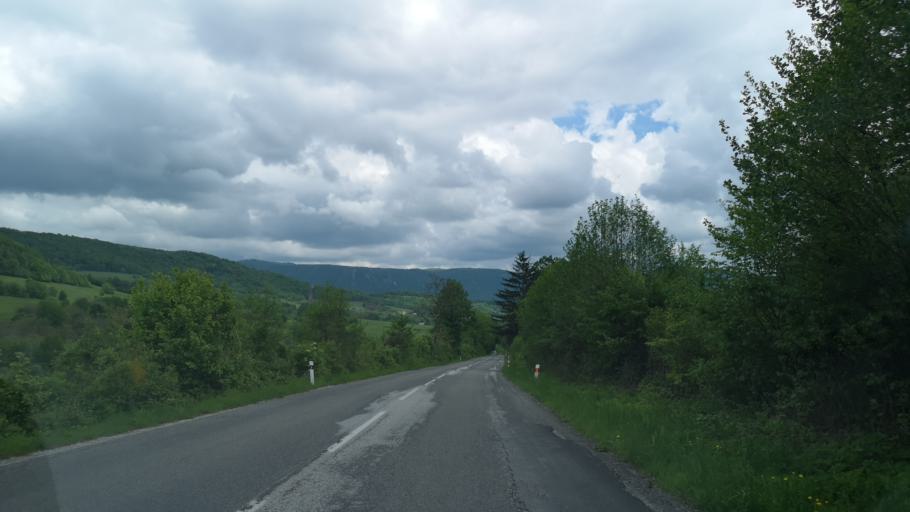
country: SK
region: Kosicky
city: Dobsina
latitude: 48.6382
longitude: 20.3221
